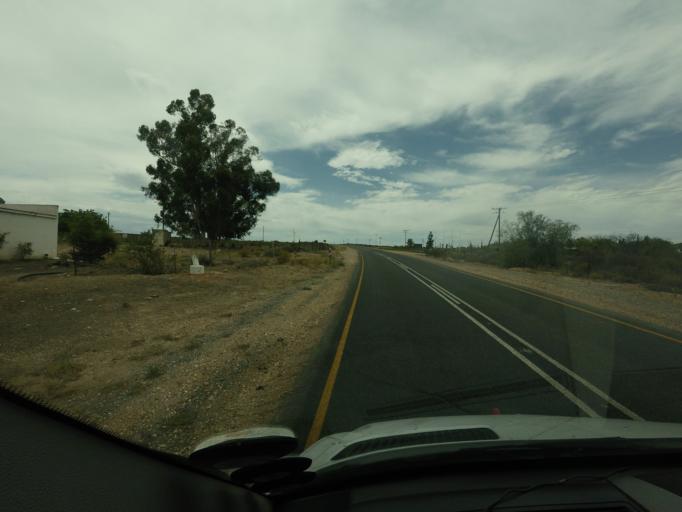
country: ZA
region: Western Cape
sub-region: Overberg District Municipality
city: Swellendam
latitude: -33.8485
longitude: 20.8575
